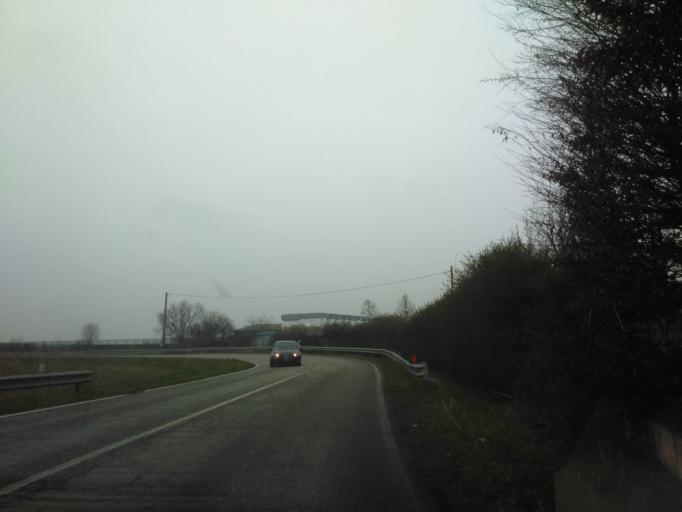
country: IT
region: Lombardy
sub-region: Provincia di Brescia
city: Longhena
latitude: 45.4309
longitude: 10.0344
